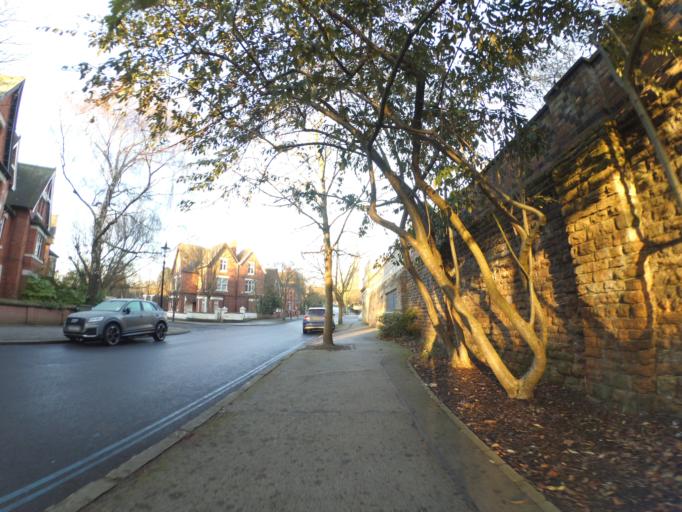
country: GB
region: England
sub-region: Nottingham
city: Nottingham
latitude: 52.9492
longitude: -1.1560
